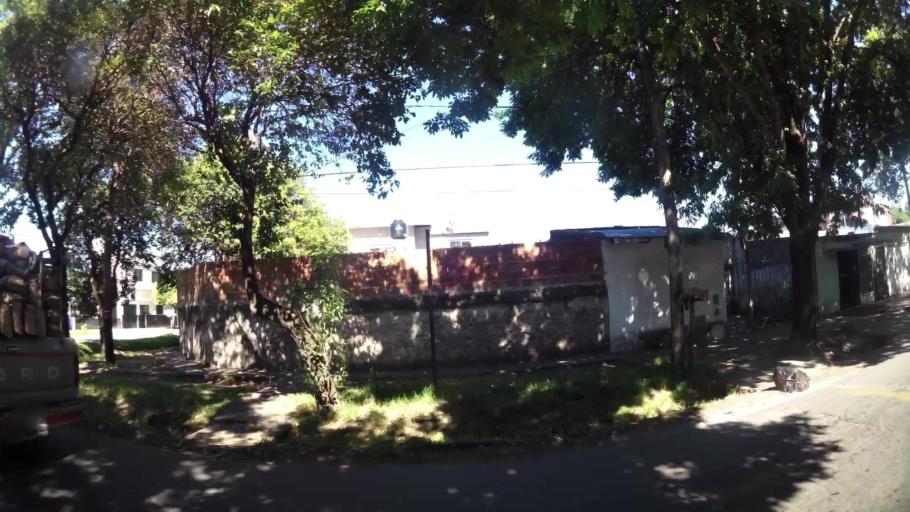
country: AR
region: Santa Fe
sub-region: Departamento de Rosario
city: Rosario
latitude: -32.9610
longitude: -60.6939
